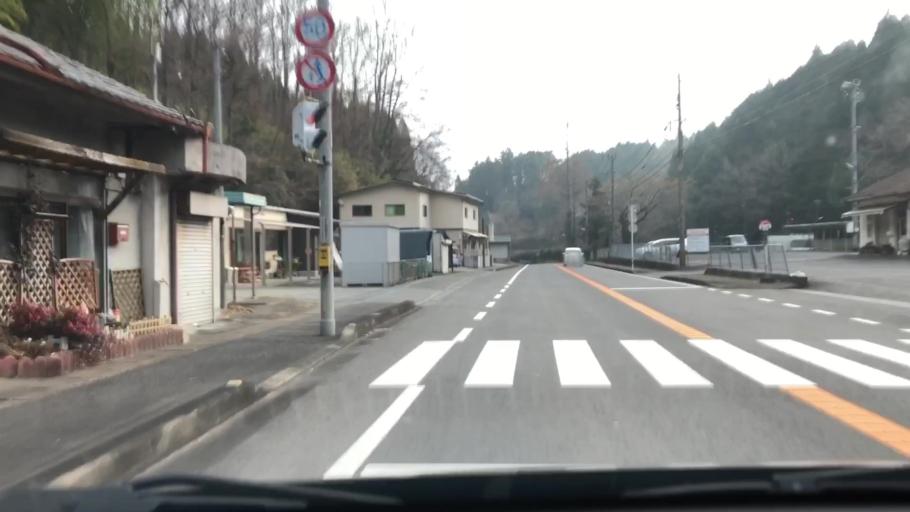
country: JP
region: Oita
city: Takedamachi
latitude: 32.9732
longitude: 131.5232
